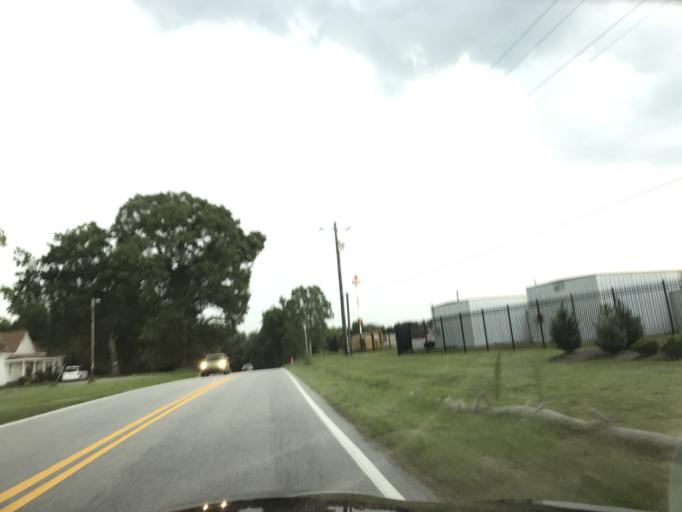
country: US
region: North Carolina
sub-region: Johnston County
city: Wilsons Mills
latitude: 35.5486
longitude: -78.3901
